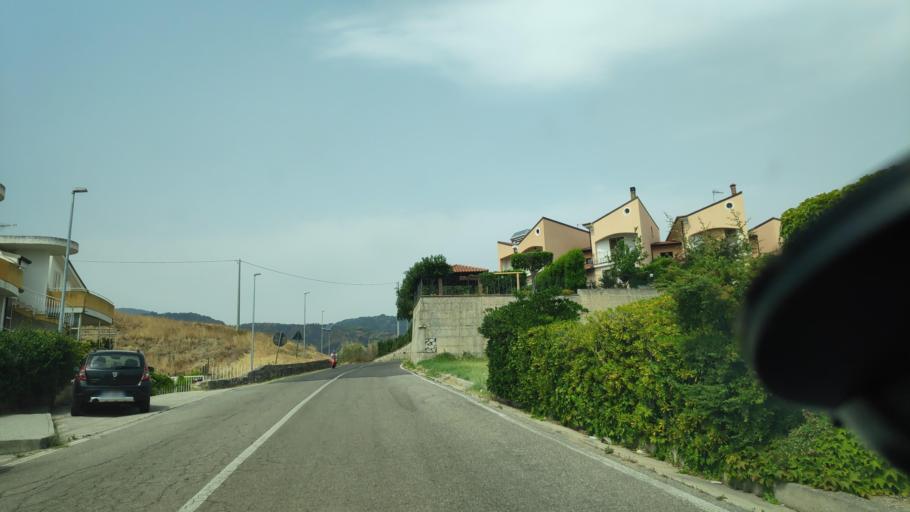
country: IT
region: Calabria
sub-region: Provincia di Catanzaro
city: Marina di Davoli
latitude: 38.6512
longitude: 16.5448
